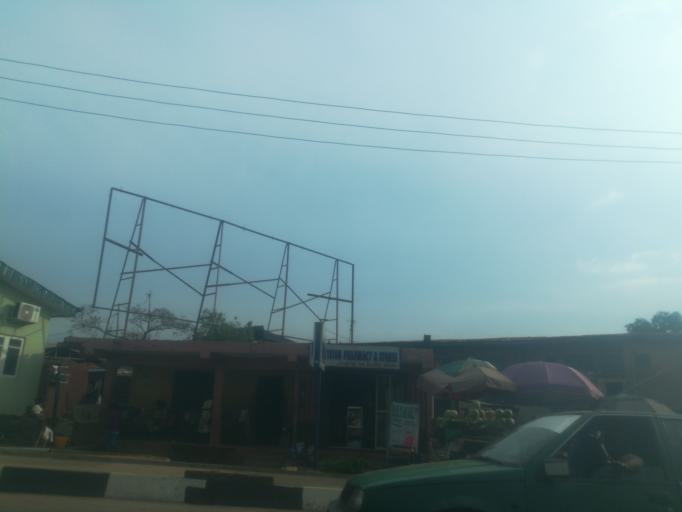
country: NG
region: Ogun
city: Abeokuta
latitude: 7.1474
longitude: 3.3293
